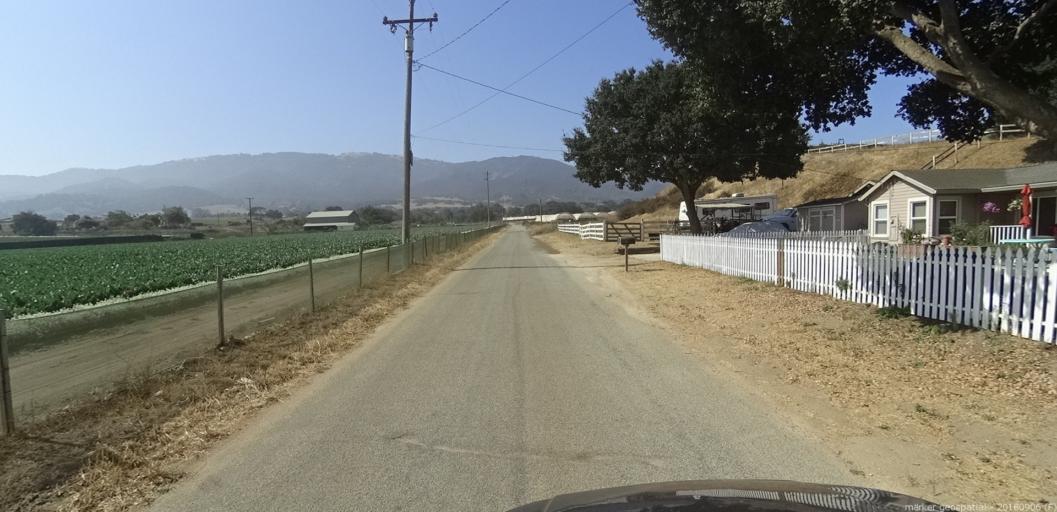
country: US
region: California
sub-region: Monterey County
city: Chualar
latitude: 36.5882
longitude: -121.6054
